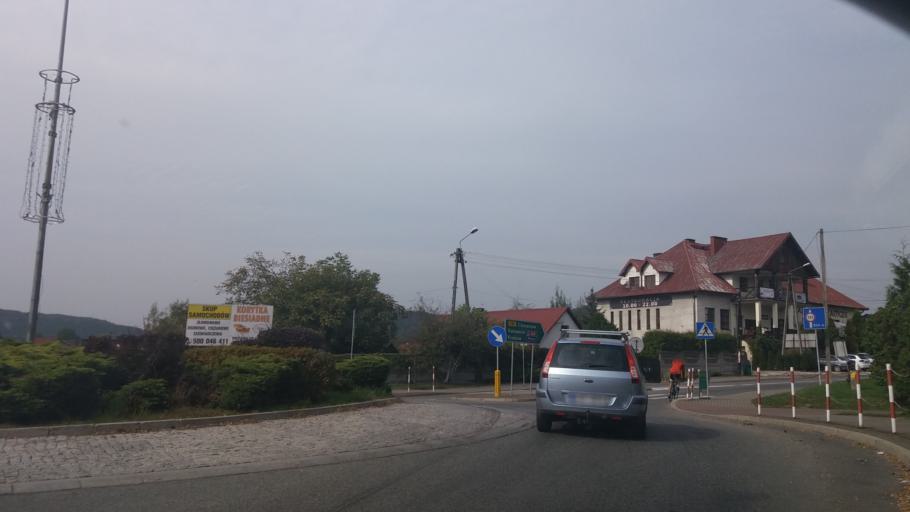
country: PL
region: Lesser Poland Voivodeship
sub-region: Powiat chrzanowski
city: Babice
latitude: 50.0746
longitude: 19.4365
